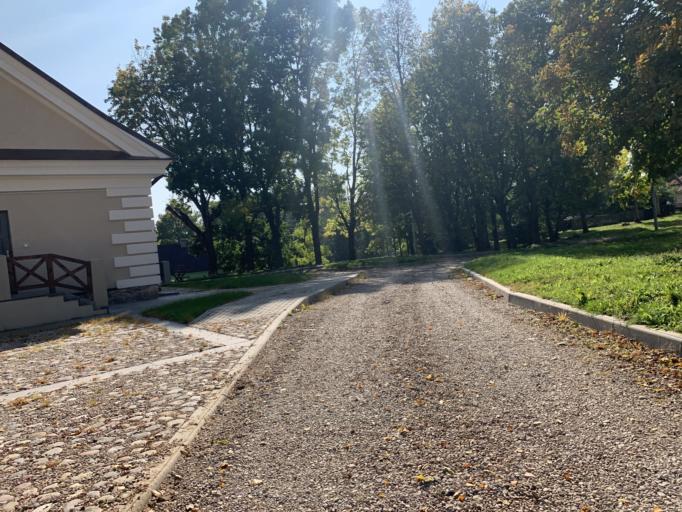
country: BY
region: Minsk
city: Rakaw
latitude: 53.8760
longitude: 26.9702
